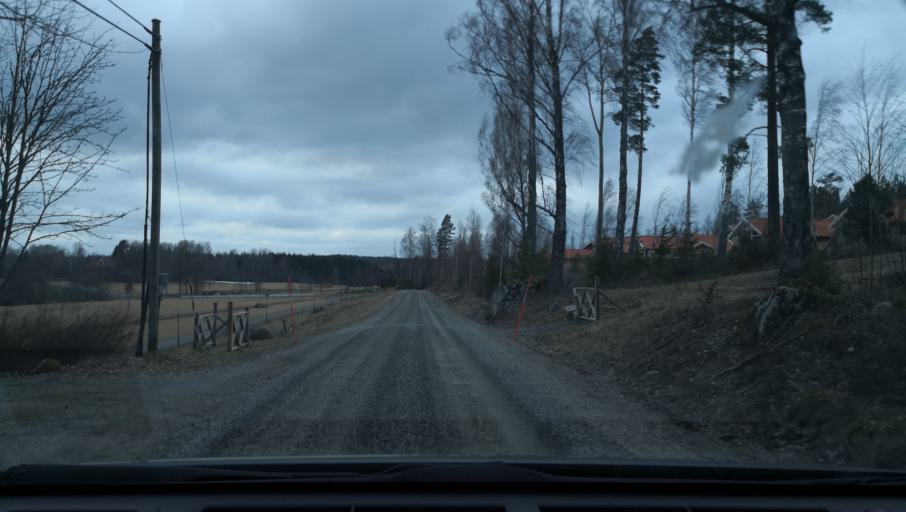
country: SE
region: Vaestmanland
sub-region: Kopings Kommun
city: Kolsva
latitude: 59.6016
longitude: 15.7025
